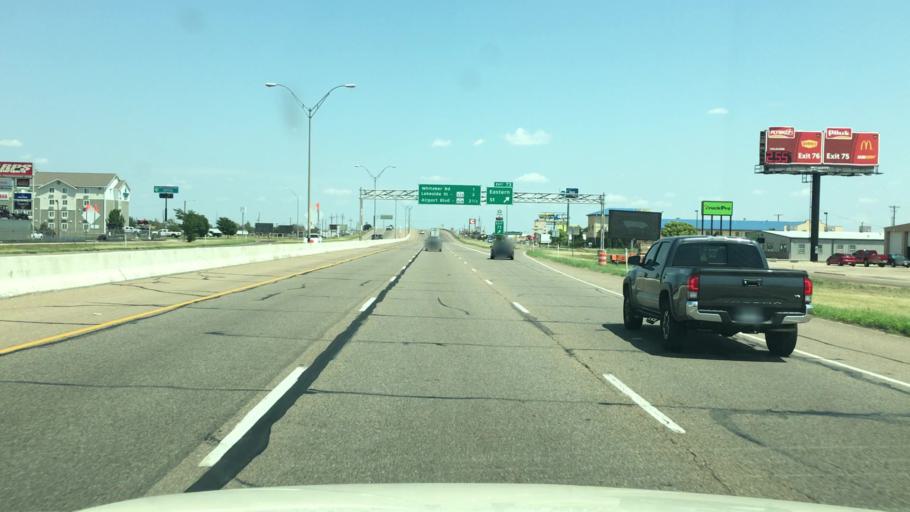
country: US
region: Texas
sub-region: Potter County
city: Amarillo
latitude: 35.1925
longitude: -101.7842
